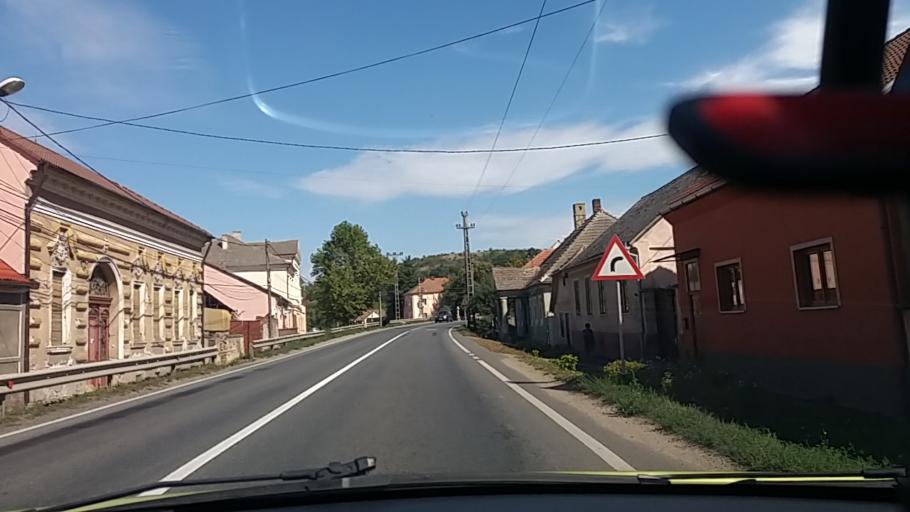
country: RO
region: Arad
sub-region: Oras Lipova
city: Radna
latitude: 46.0965
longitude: 21.6873
